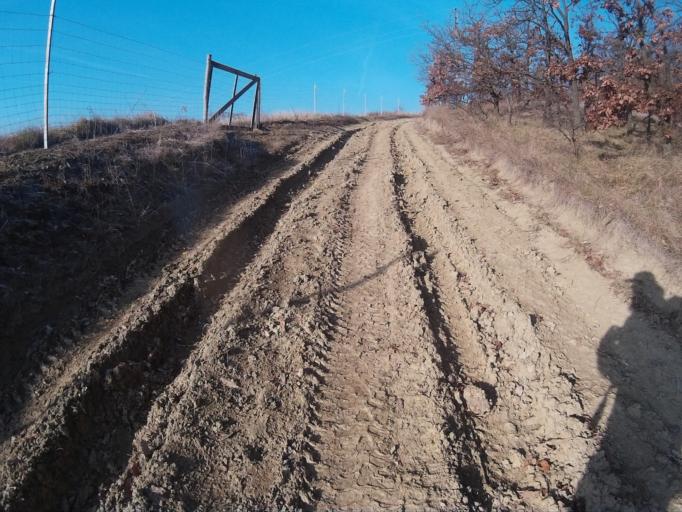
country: HU
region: Nograd
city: Bercel
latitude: 47.9313
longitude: 19.4115
